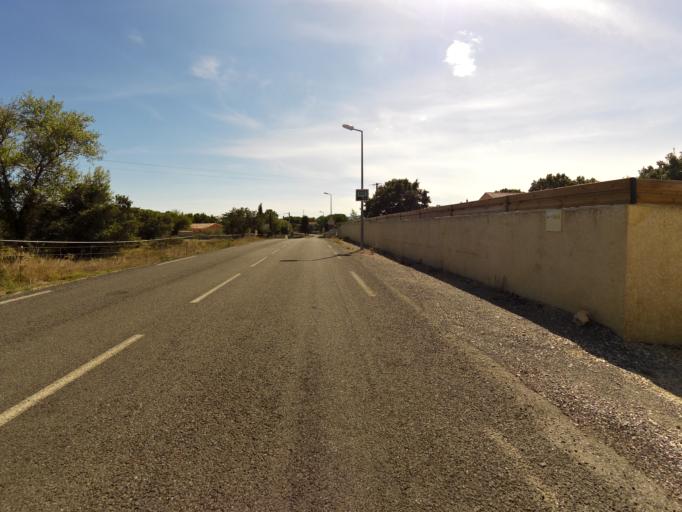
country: FR
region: Languedoc-Roussillon
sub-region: Departement du Gard
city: Quissac
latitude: 43.9576
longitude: 4.0352
